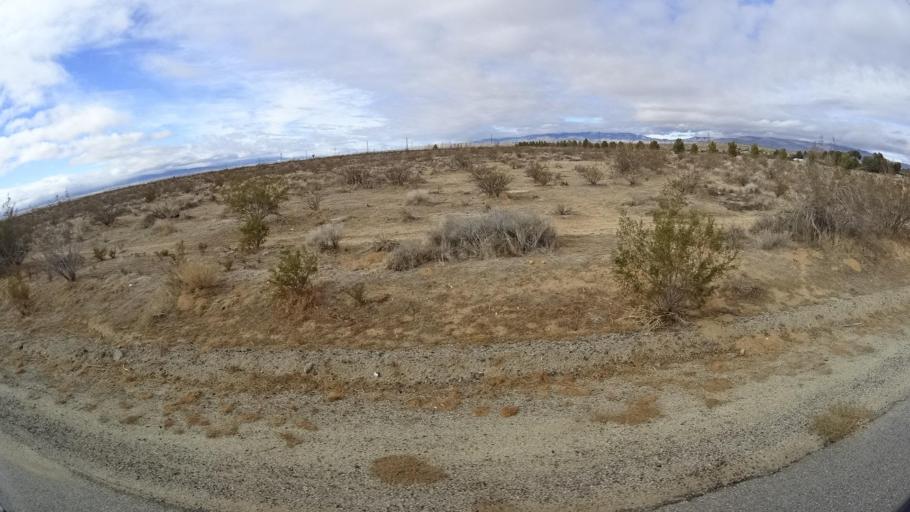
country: US
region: California
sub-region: Kern County
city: Rosamond
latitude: 34.8739
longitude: -118.2911
